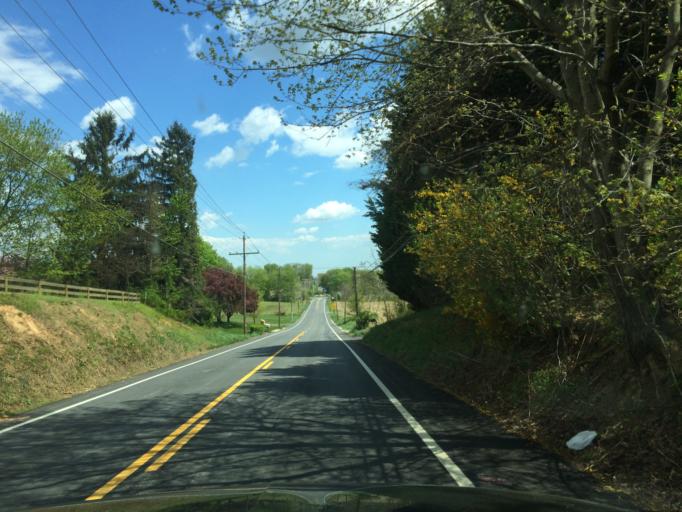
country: US
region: Maryland
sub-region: Carroll County
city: Eldersburg
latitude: 39.4315
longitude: -77.0118
